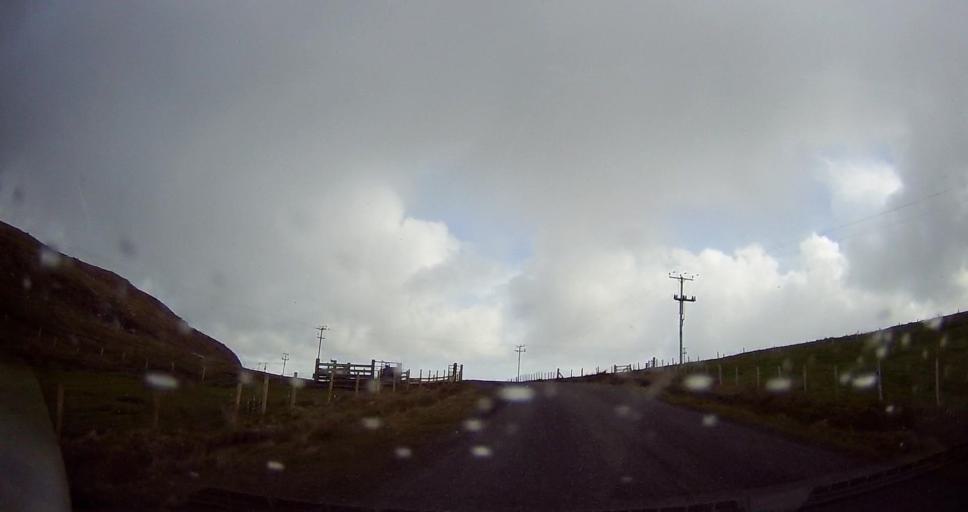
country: GB
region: Scotland
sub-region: Shetland Islands
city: Lerwick
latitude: 60.5420
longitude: -1.3456
